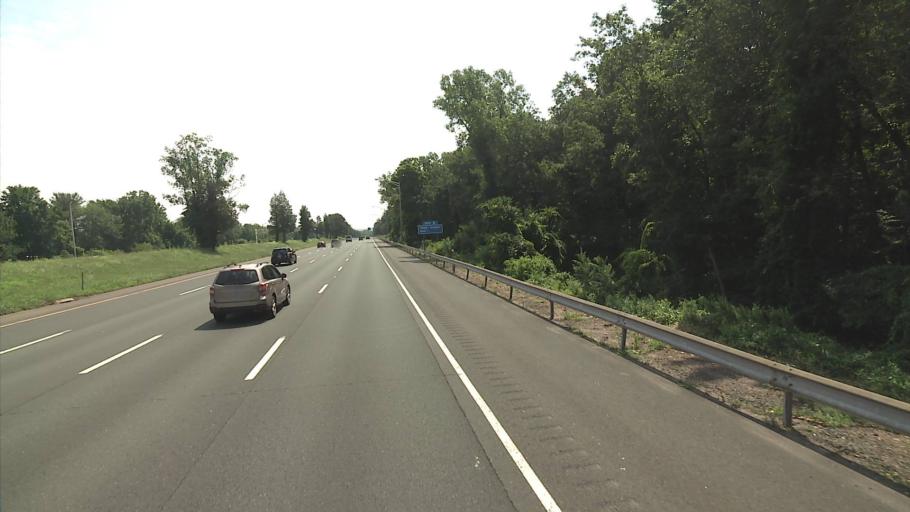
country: US
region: Connecticut
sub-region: Hartford County
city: Manchester
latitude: 41.7645
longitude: -72.5618
